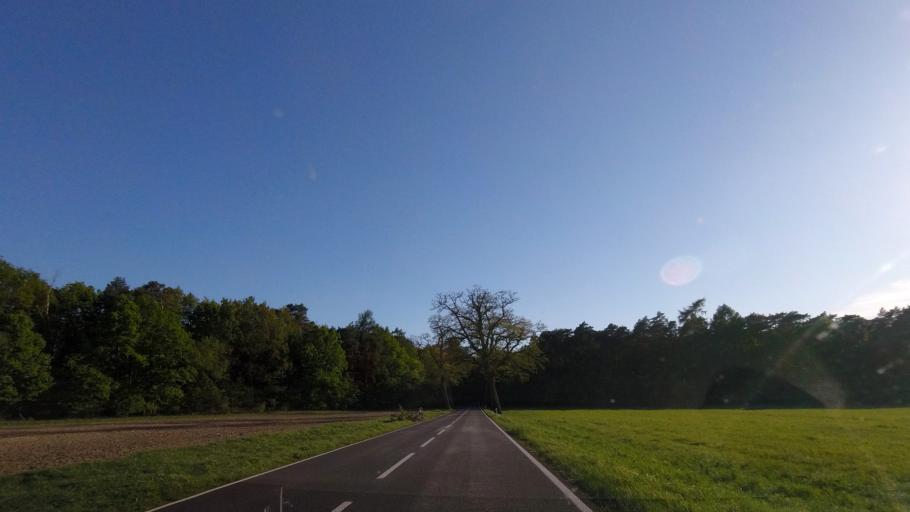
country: DE
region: Brandenburg
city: Baruth
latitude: 52.0072
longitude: 13.4435
